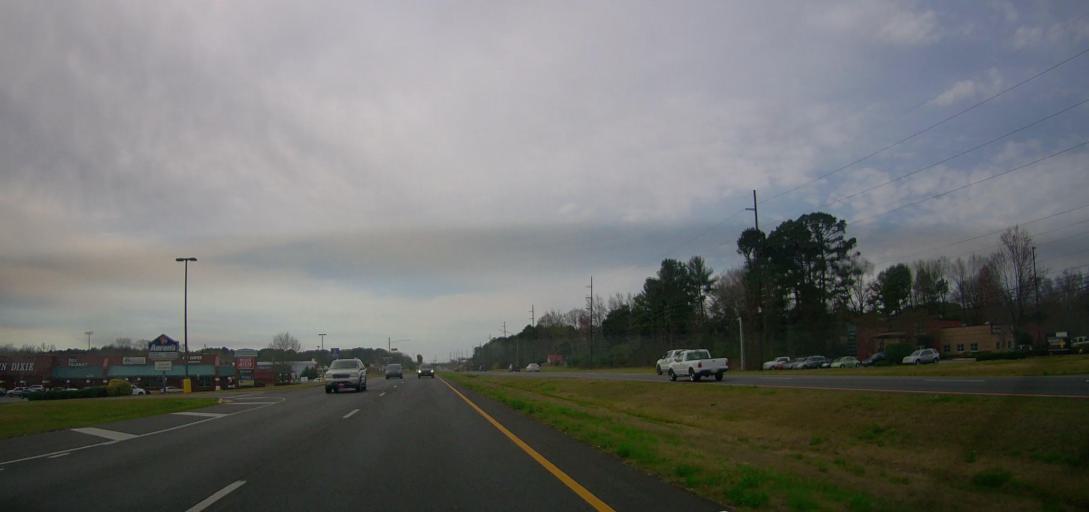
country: US
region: Alabama
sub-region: Walker County
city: Jasper
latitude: 33.8427
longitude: -87.2438
